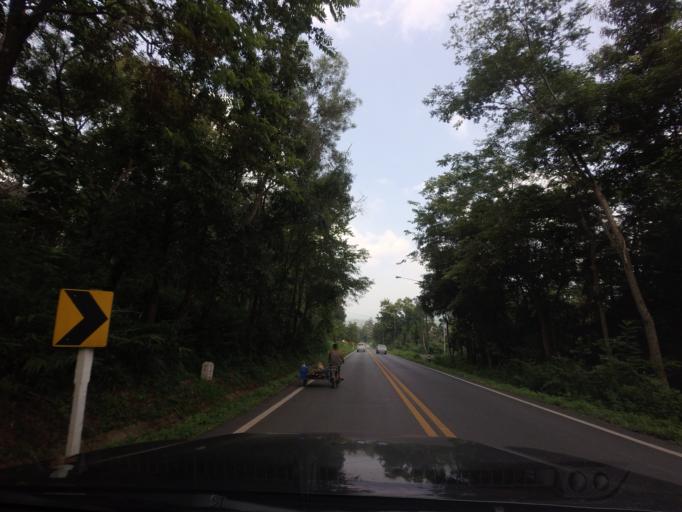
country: TH
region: Nan
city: Pua
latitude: 19.1372
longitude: 100.9485
